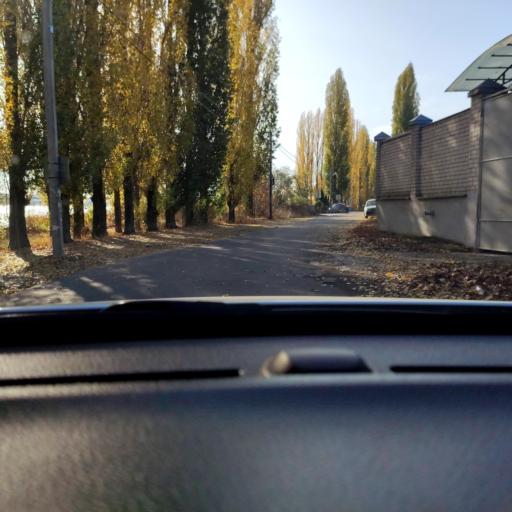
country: RU
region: Voronezj
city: Voronezh
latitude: 51.7006
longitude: 39.2365
